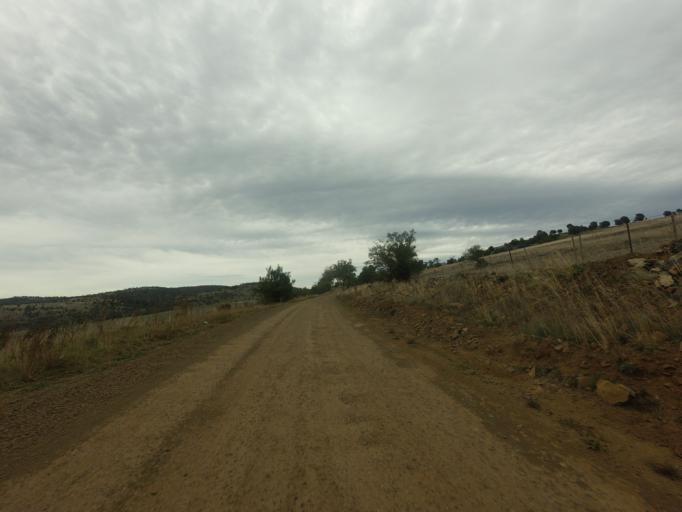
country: AU
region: Tasmania
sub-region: Derwent Valley
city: New Norfolk
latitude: -42.5521
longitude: 146.9020
